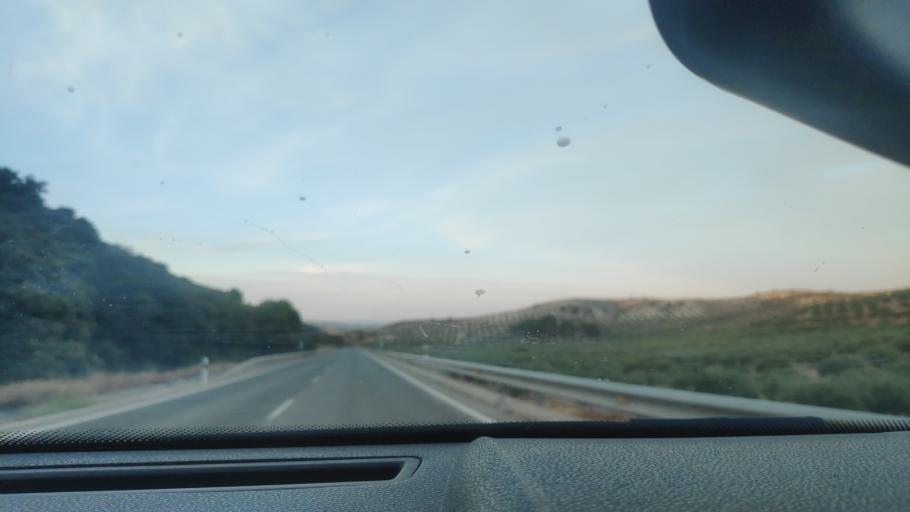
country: ES
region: Andalusia
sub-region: Provincia de Jaen
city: Escanuela
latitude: 37.8354
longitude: -4.0474
